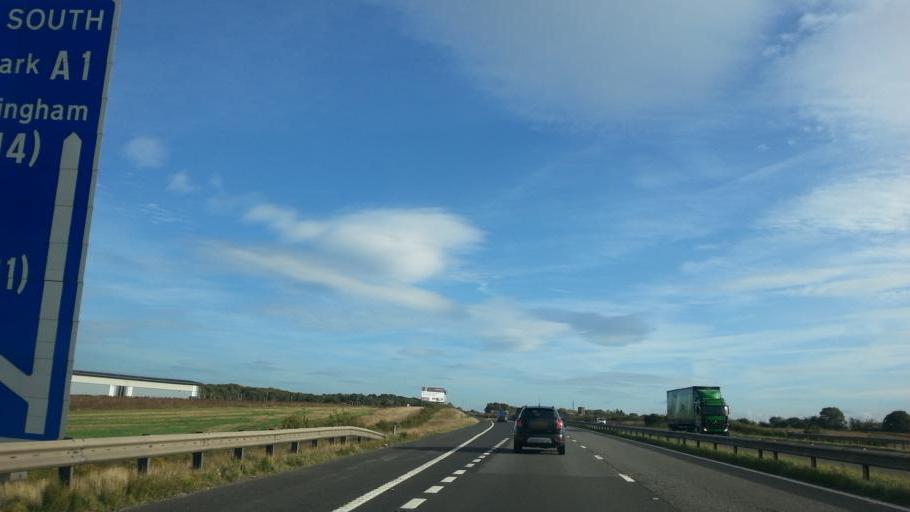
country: GB
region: England
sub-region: Nottinghamshire
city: Bircotes
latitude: 53.3925
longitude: -1.0708
